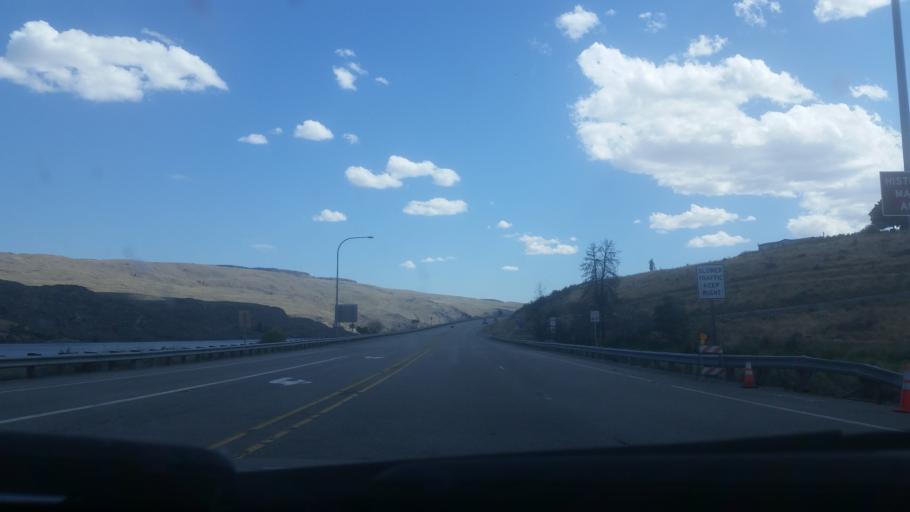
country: US
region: Washington
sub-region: Okanogan County
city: Brewster
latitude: 48.0483
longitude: -119.9014
